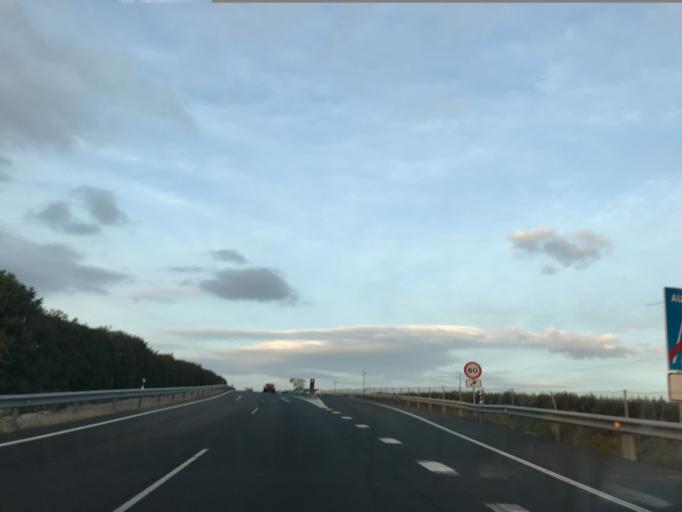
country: ES
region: Andalusia
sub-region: Province of Cordoba
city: La Victoria
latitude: 37.7558
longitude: -4.8309
